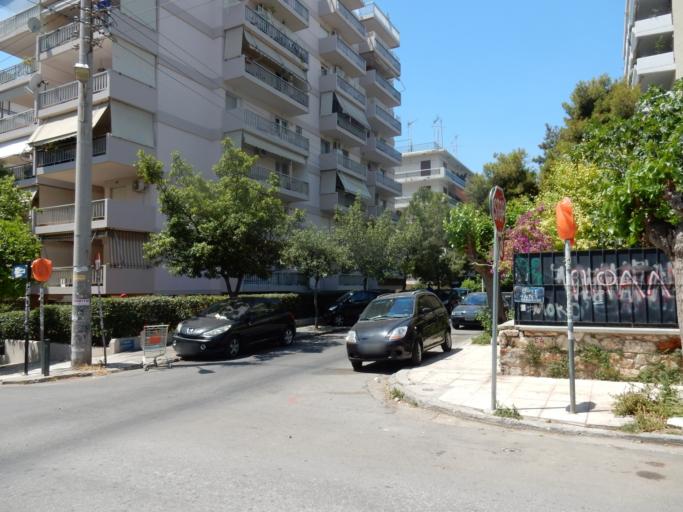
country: GR
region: Attica
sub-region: Nomarchia Athinas
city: Palaio Faliro
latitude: 37.9254
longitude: 23.6960
